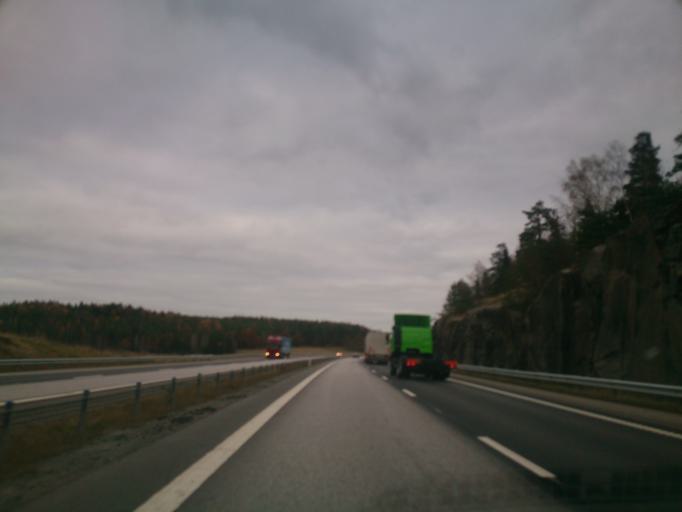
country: SE
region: Soedermanland
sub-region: Oxelosunds Kommun
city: Oxelosund
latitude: 58.8467
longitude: 17.1942
